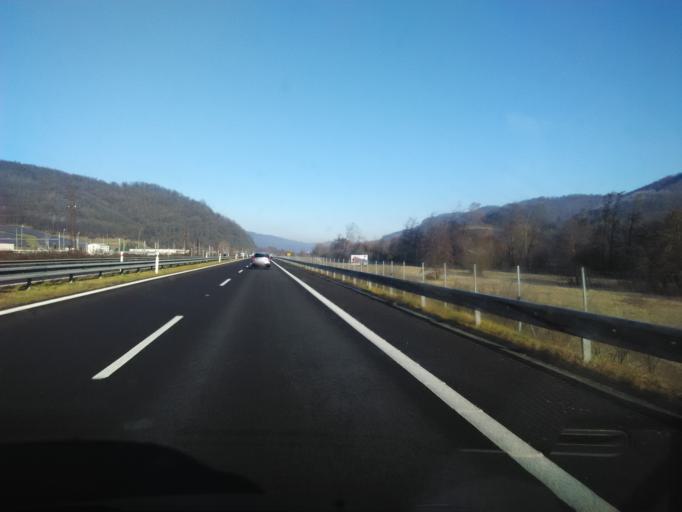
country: SK
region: Banskobystricky
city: Zarnovica
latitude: 48.4884
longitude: 18.7304
